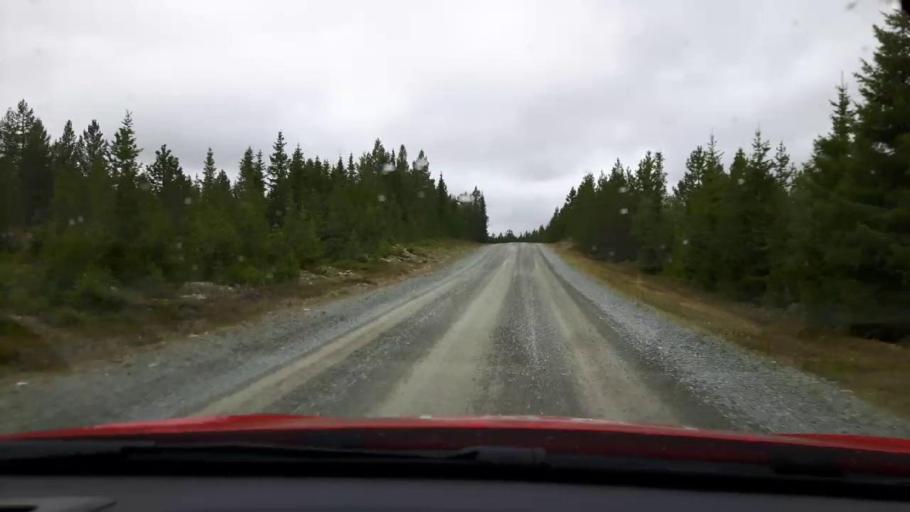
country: SE
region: Jaemtland
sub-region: Bergs Kommun
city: Hoverberg
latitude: 62.9044
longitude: 14.0683
